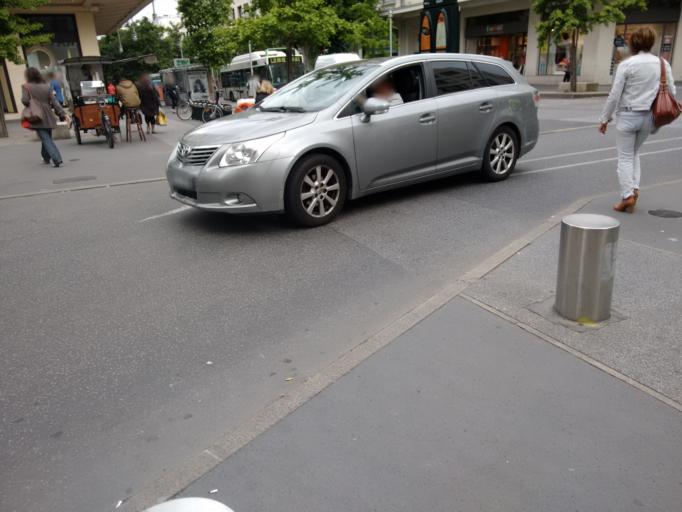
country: FR
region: Pays de la Loire
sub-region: Departement de la Loire-Atlantique
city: Nantes
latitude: 47.2157
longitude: -1.5611
